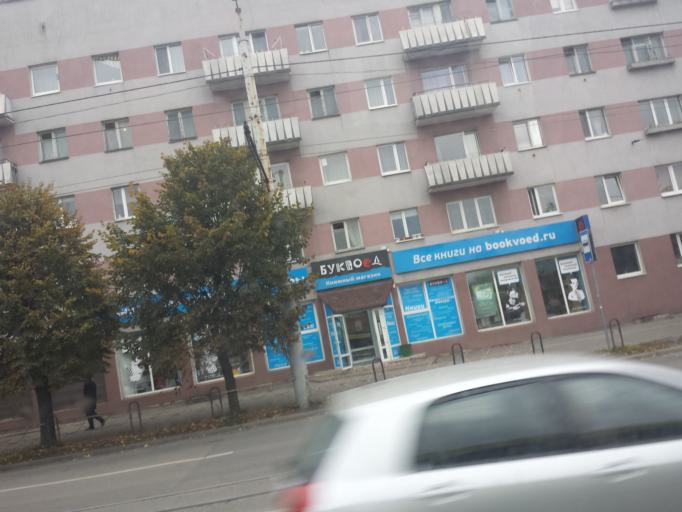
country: RU
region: Kaliningrad
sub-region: Gorod Kaliningrad
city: Kaliningrad
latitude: 54.6955
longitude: 20.5009
